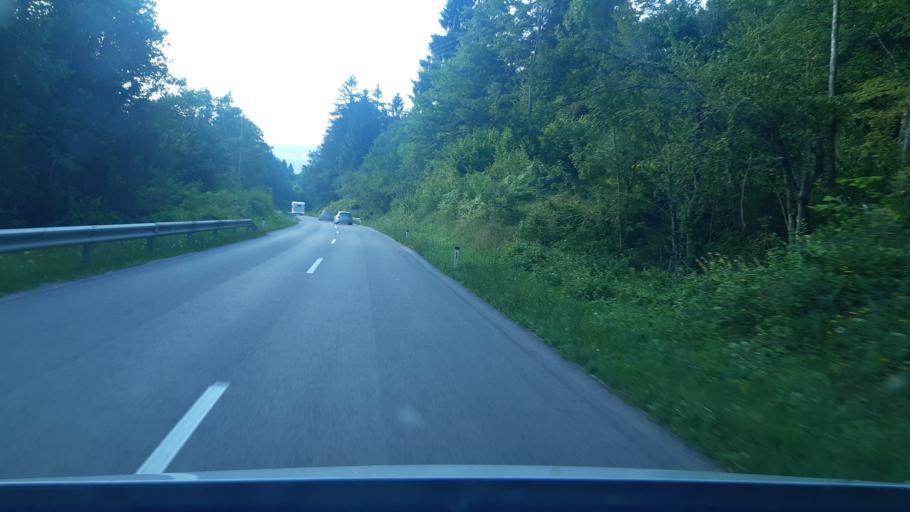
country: SI
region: Semic
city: Semic
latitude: 45.6567
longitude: 15.1183
